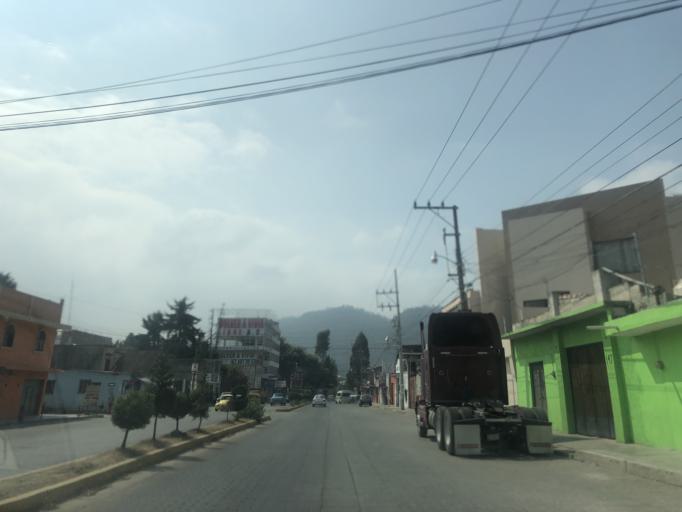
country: MX
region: Chiapas
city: San Cristobal de las Casas
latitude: 16.7145
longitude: -92.6348
